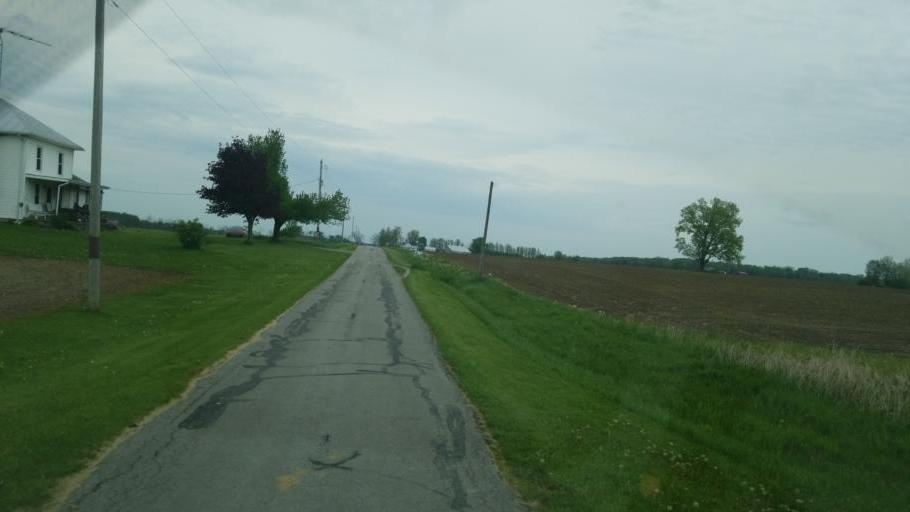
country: US
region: Ohio
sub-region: Huron County
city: Willard
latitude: 41.0087
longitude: -82.8380
